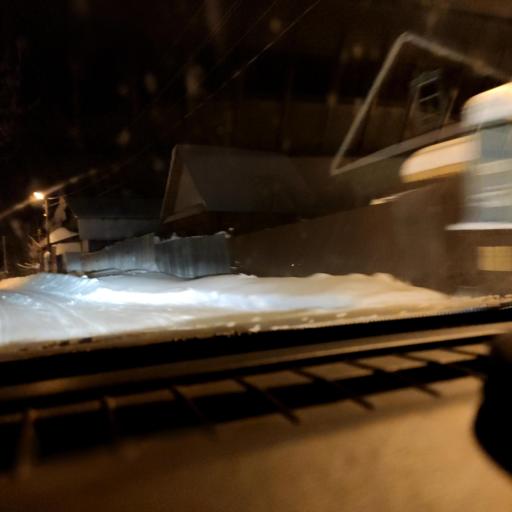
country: RU
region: Perm
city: Perm
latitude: 58.0412
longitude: 56.3564
